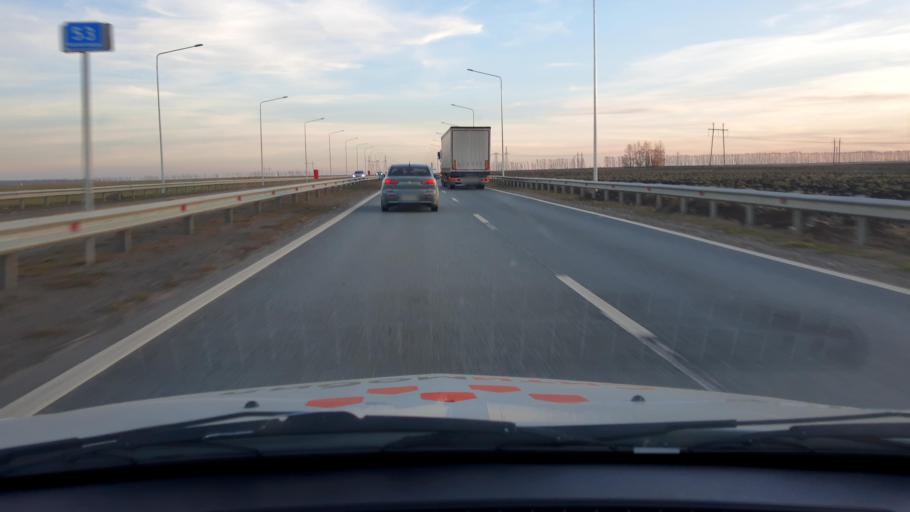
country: RU
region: Bashkortostan
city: Tolbazy
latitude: 54.2593
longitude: 55.8827
